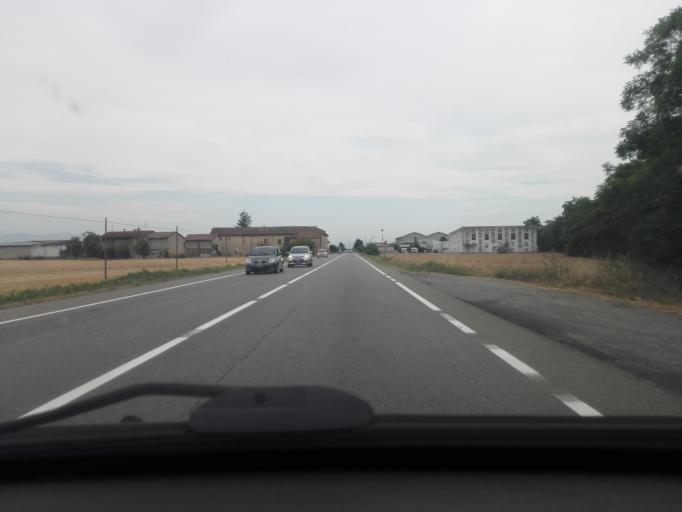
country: IT
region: Piedmont
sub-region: Provincia di Alessandria
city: Mandrogne
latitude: 44.8442
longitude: 8.7265
